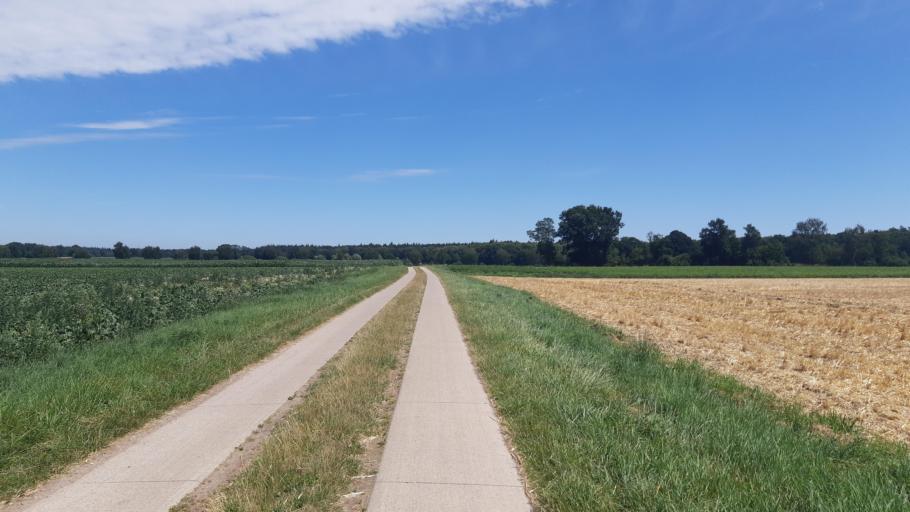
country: DE
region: Lower Saxony
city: Tosterglope
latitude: 53.2314
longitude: 10.7894
